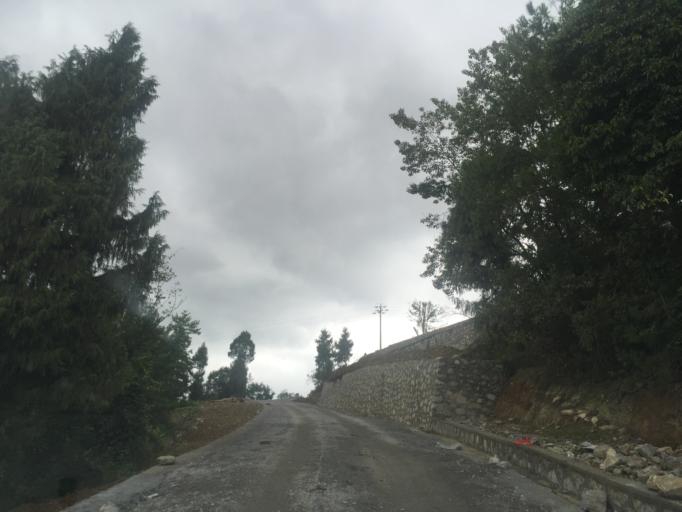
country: CN
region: Guizhou Sheng
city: Shiqian
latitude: 27.6782
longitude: 108.1126
